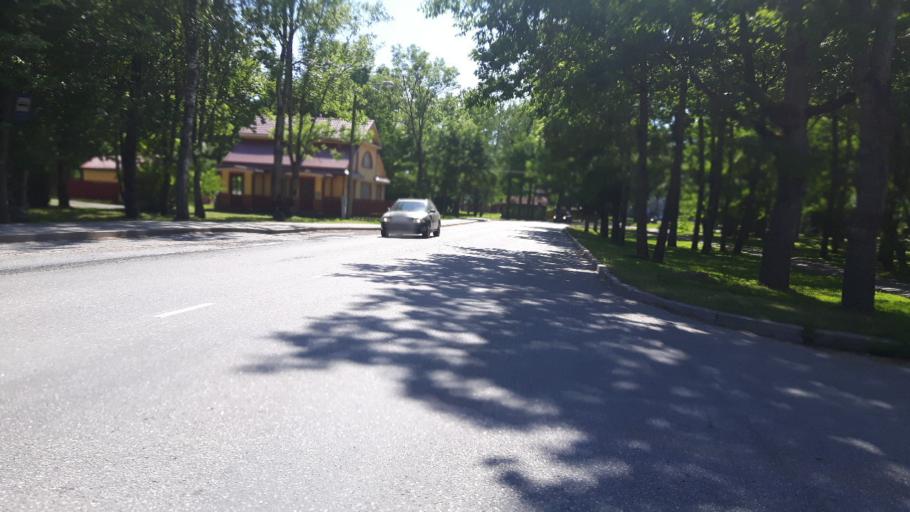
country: EE
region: Paernumaa
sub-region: Sindi linn
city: Sindi
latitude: 58.4078
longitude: 24.6581
